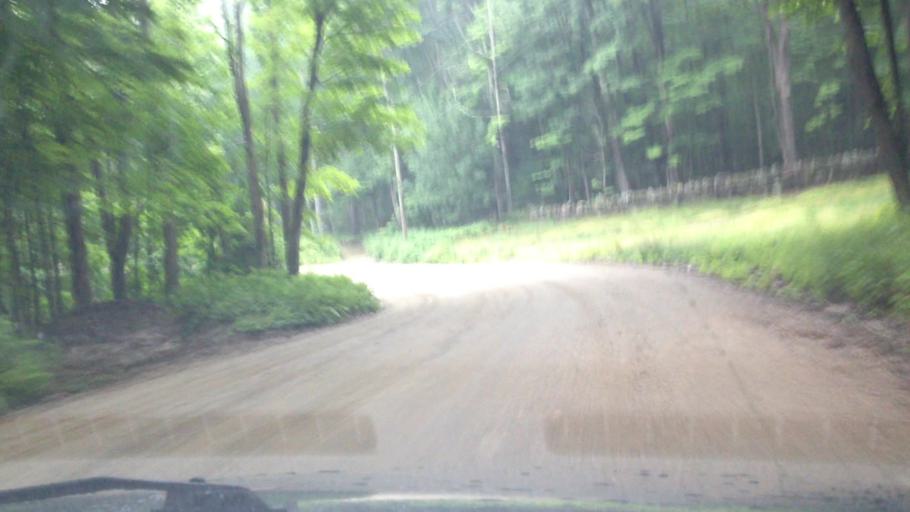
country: US
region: New Hampshire
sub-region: Cheshire County
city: Marlborough
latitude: 42.8951
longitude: -72.1597
